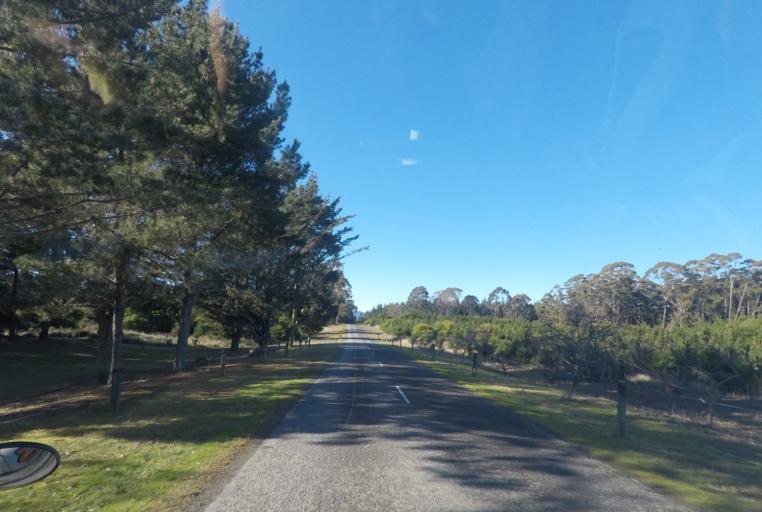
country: NZ
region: Tasman
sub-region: Tasman District
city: Mapua
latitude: -41.2666
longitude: 173.1482
